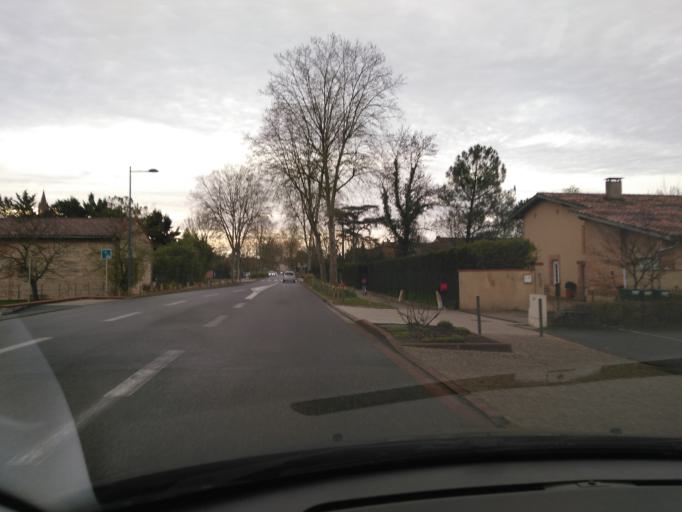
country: FR
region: Midi-Pyrenees
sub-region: Departement de la Haute-Garonne
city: Castelnau-d'Estretefonds
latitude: 43.7865
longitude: 1.3529
